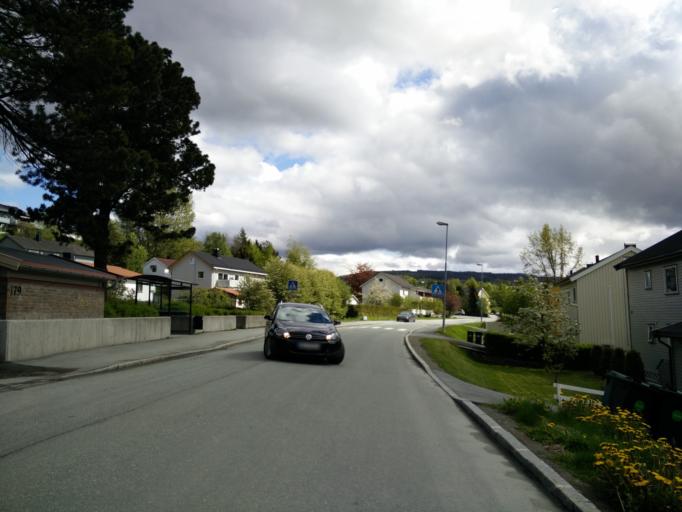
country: NO
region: Sor-Trondelag
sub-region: Trondheim
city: Trondheim
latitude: 63.4039
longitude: 10.4049
